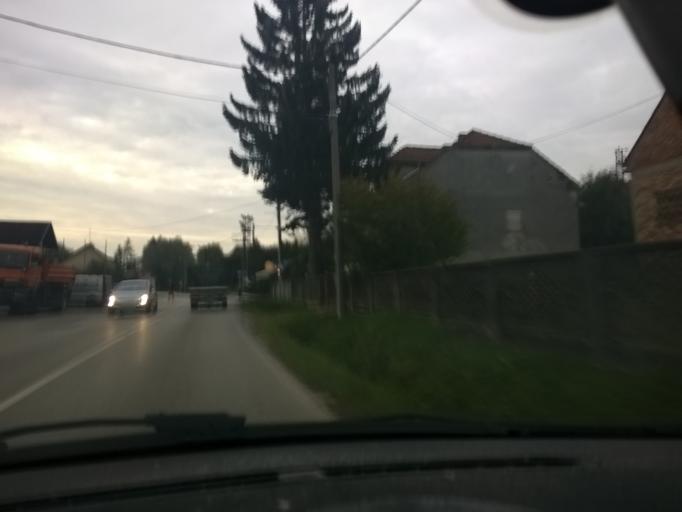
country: HR
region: Zagrebacka
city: Pojatno
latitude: 45.9080
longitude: 15.8071
